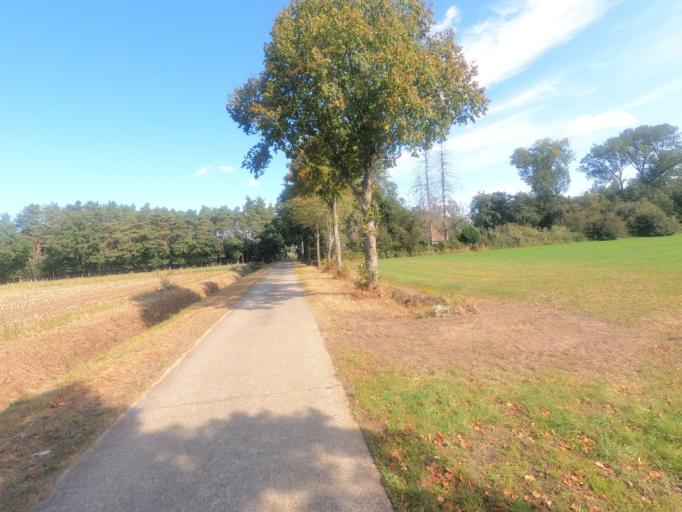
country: BE
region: Flanders
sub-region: Provincie Antwerpen
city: Lille
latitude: 51.2488
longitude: 4.8462
